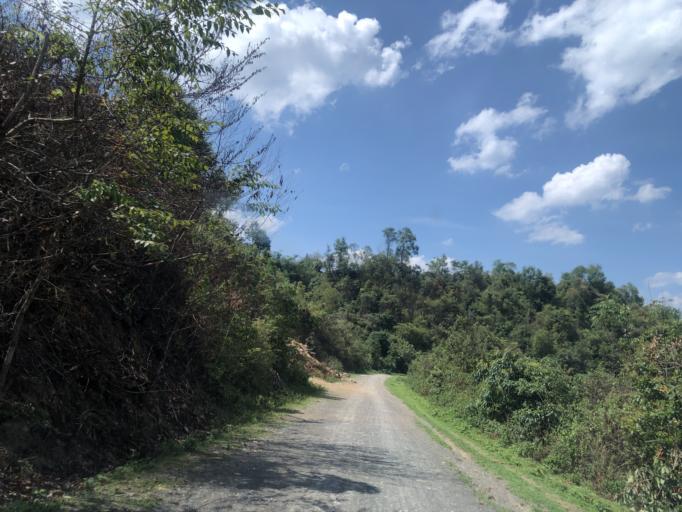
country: LA
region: Phongsali
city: Phongsali
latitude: 21.4192
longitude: 102.2511
